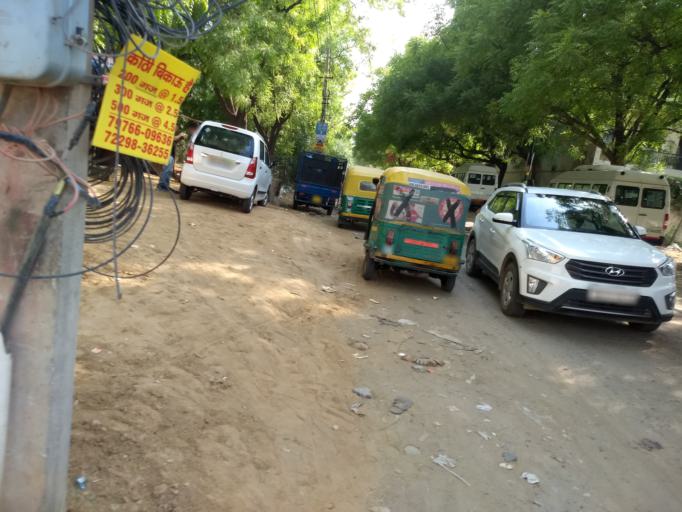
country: IN
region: Haryana
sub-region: Gurgaon
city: Gurgaon
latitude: 28.4451
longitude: 77.0630
